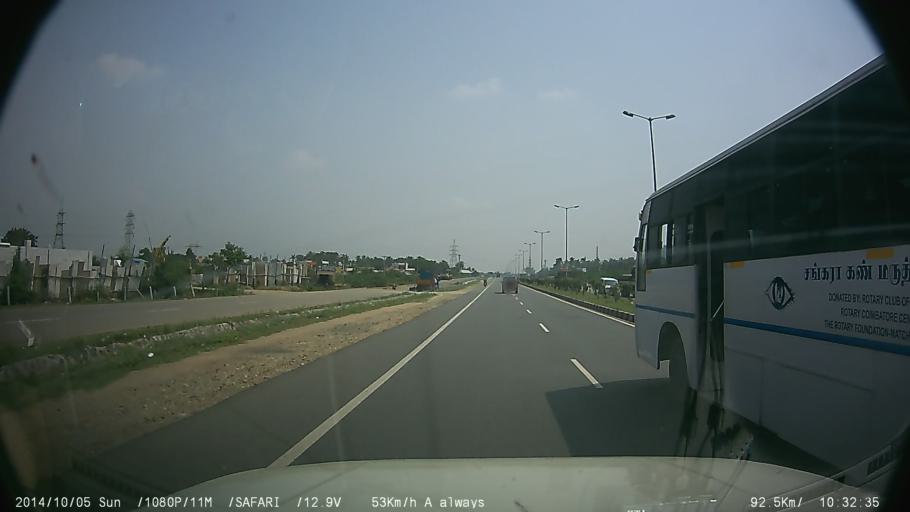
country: IN
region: Tamil Nadu
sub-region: Salem
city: Salem
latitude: 11.6370
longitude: 78.1702
